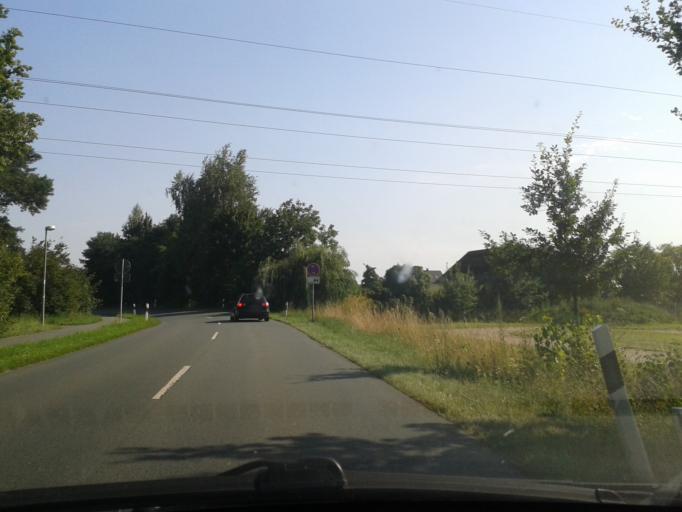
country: DE
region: North Rhine-Westphalia
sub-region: Regierungsbezirk Detmold
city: Hovelhof
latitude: 51.7491
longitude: 8.6687
